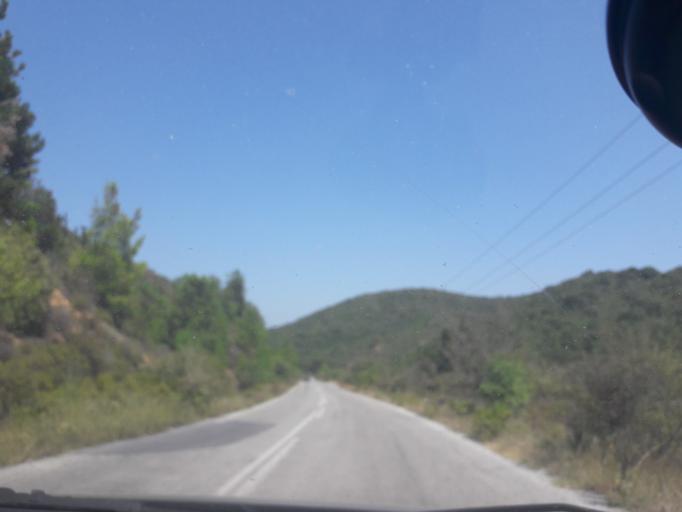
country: GR
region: Central Macedonia
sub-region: Nomos Chalkidikis
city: Megali Panagia
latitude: 40.3821
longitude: 23.7425
